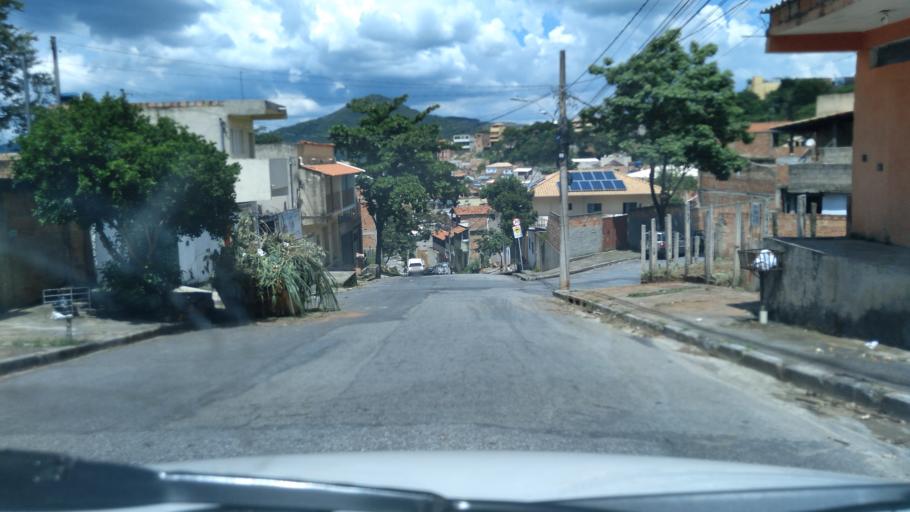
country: BR
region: Minas Gerais
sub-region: Belo Horizonte
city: Belo Horizonte
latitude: -19.8600
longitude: -43.8746
